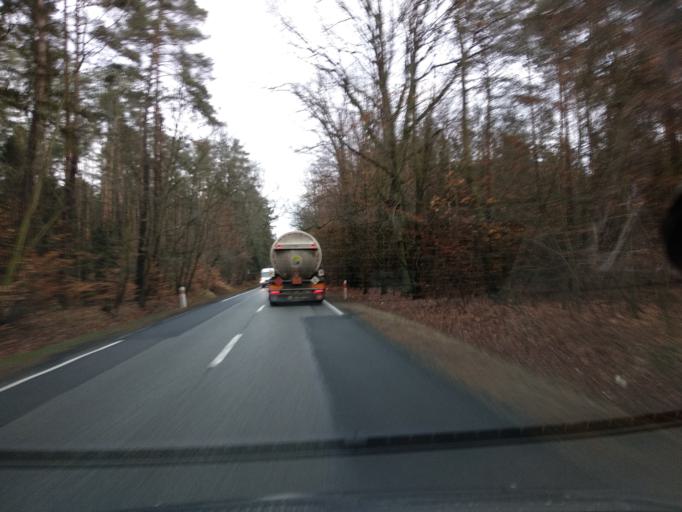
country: PL
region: Lower Silesian Voivodeship
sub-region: Powiat olesnicki
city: Twardogora
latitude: 51.3211
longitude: 17.5660
